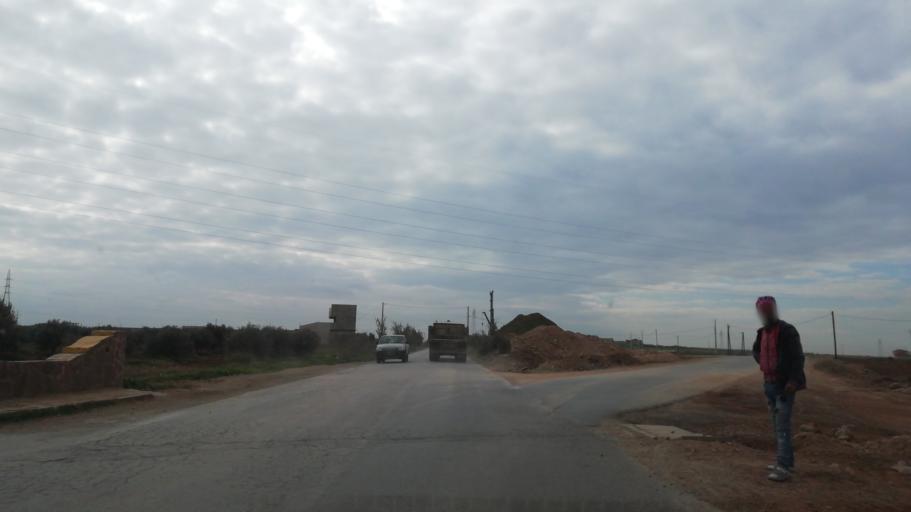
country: DZ
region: Oran
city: Ain el Bya
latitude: 35.7913
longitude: -0.3419
